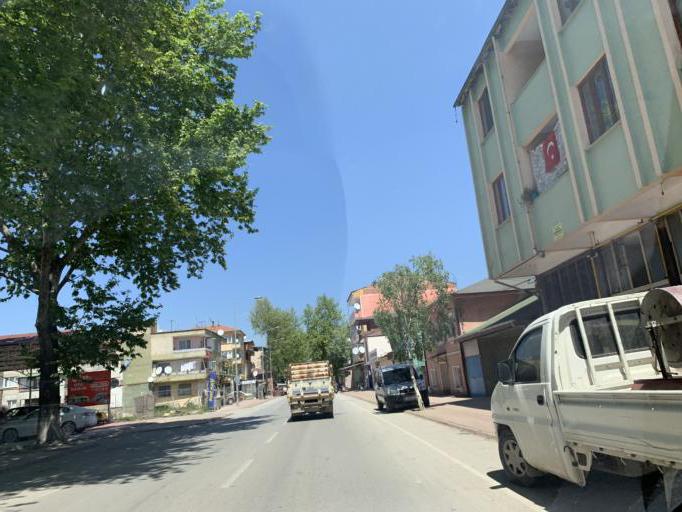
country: TR
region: Bursa
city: Iznik
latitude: 40.4250
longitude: 29.7194
